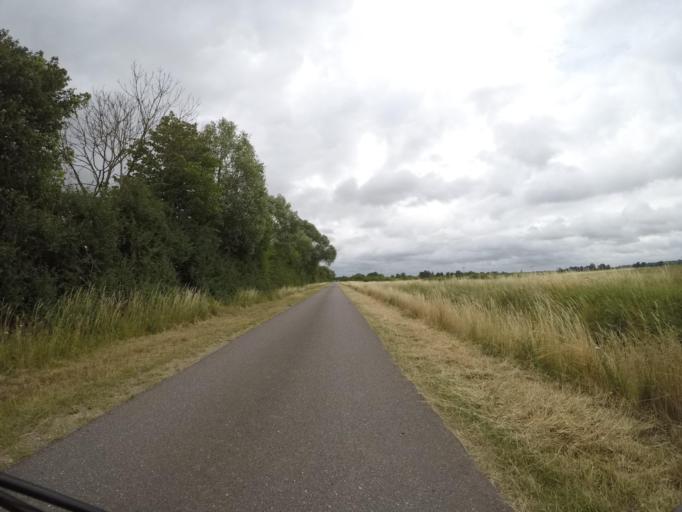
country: DE
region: Lower Saxony
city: Hitzacker
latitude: 53.1652
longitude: 11.1047
